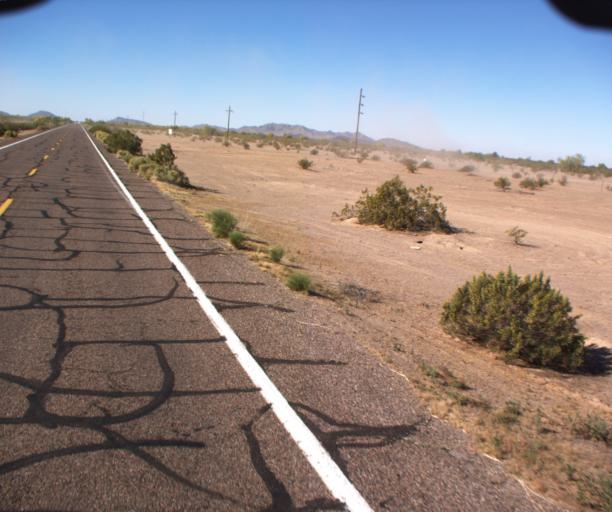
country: US
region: Arizona
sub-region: Maricopa County
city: Gila Bend
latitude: 32.8739
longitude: -112.7580
